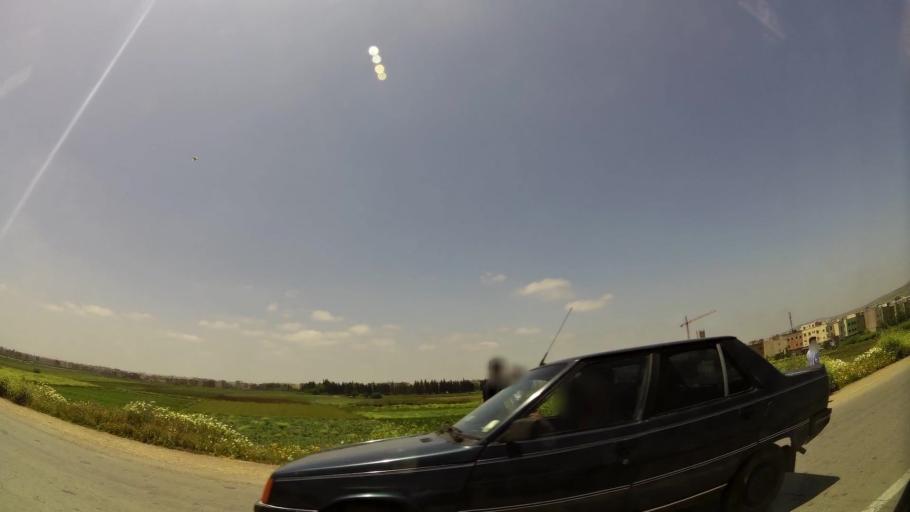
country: MA
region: Fes-Boulemane
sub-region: Fes
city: Fes
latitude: 34.0344
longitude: -5.0314
